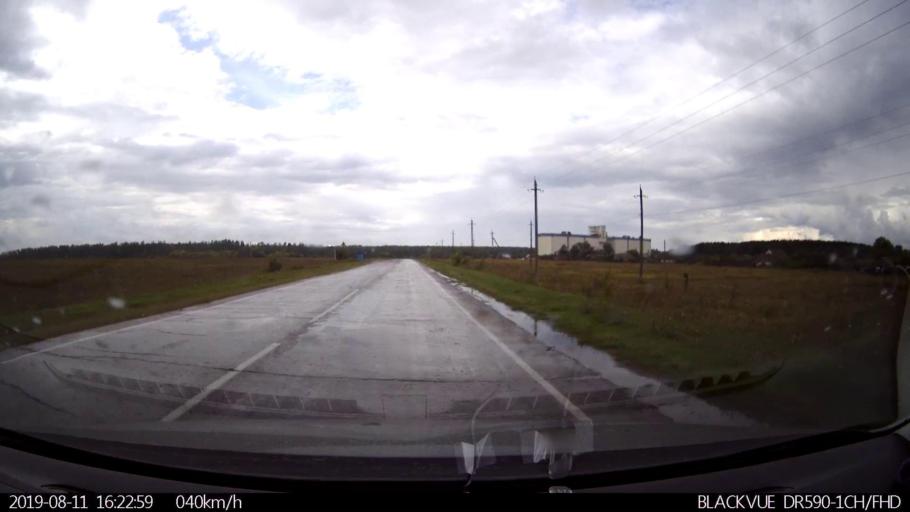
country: RU
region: Ulyanovsk
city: Mayna
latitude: 54.0919
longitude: 47.5905
